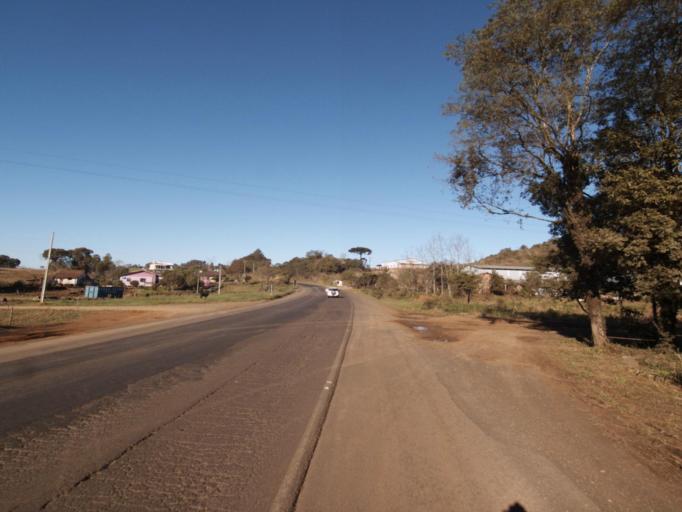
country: BR
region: Rio Grande do Sul
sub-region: Frederico Westphalen
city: Frederico Westphalen
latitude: -26.8953
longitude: -53.1900
